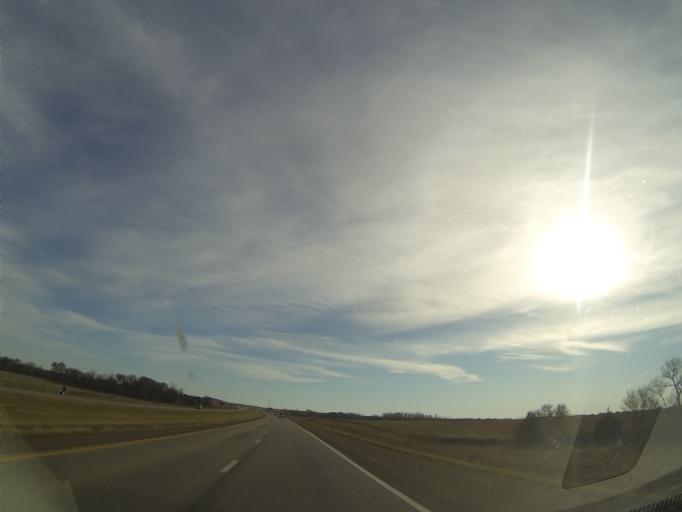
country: US
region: Kansas
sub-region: Ottawa County
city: Minneapolis
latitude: 39.0277
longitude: -97.6441
